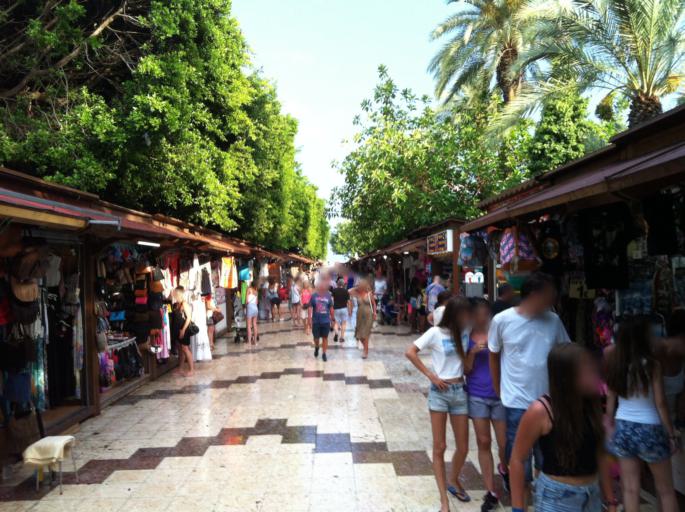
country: ES
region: Valencia
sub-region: Provincia de Alicante
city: Torrevieja
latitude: 37.9754
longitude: -0.6796
